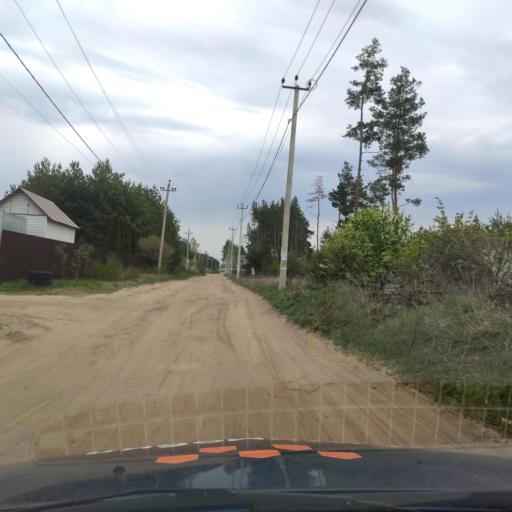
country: RU
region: Voronezj
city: Podgornoye
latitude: 51.8586
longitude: 39.1594
